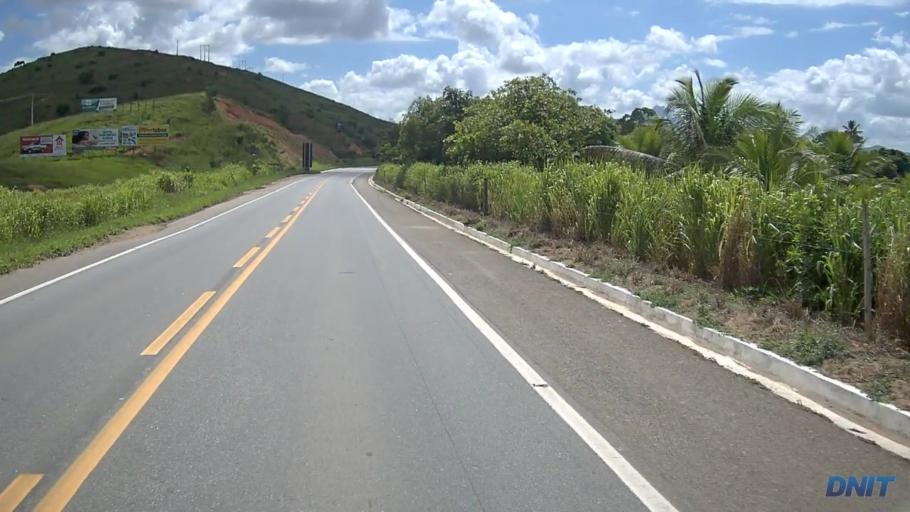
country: BR
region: Minas Gerais
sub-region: Governador Valadares
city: Governador Valadares
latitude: -18.9306
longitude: -42.0455
